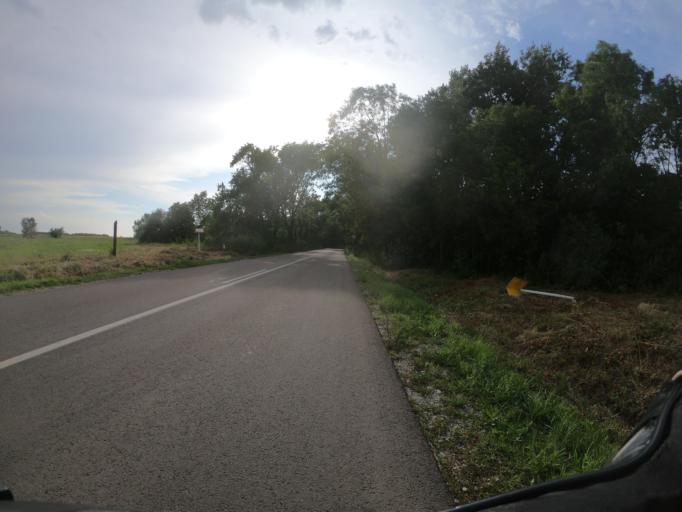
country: HU
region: Borsod-Abauj-Zemplen
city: Mezocsat
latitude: 47.8275
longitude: 20.8450
